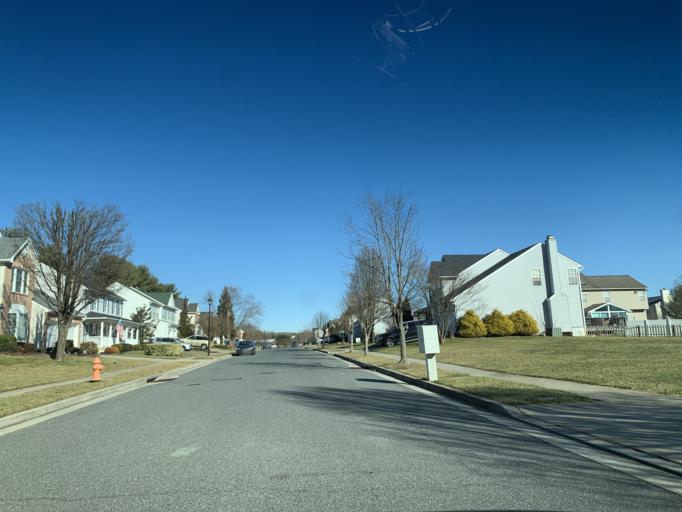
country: US
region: Maryland
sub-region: Baltimore County
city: Perry Hall
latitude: 39.4056
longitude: -76.4617
